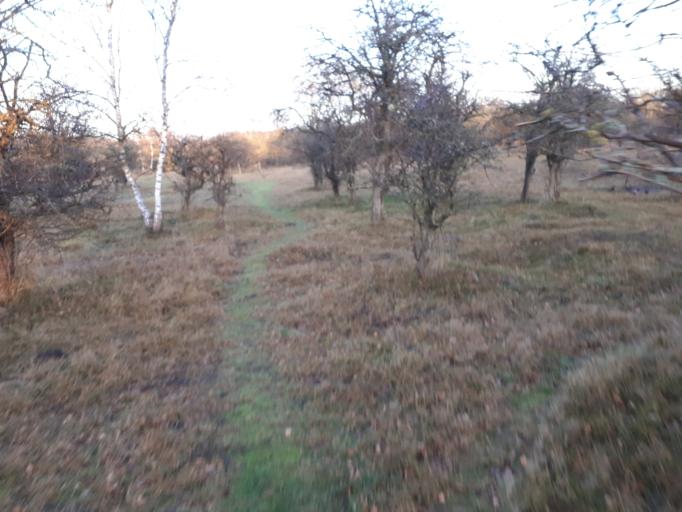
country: NL
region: South Holland
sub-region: Gemeente Wassenaar
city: Wassenaar
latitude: 52.1402
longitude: 4.3595
